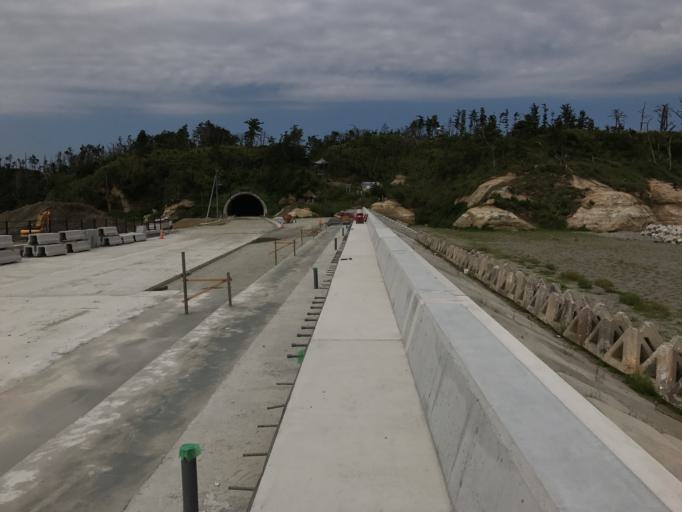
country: JP
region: Miyagi
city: Marumori
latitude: 37.8212
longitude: 140.9857
